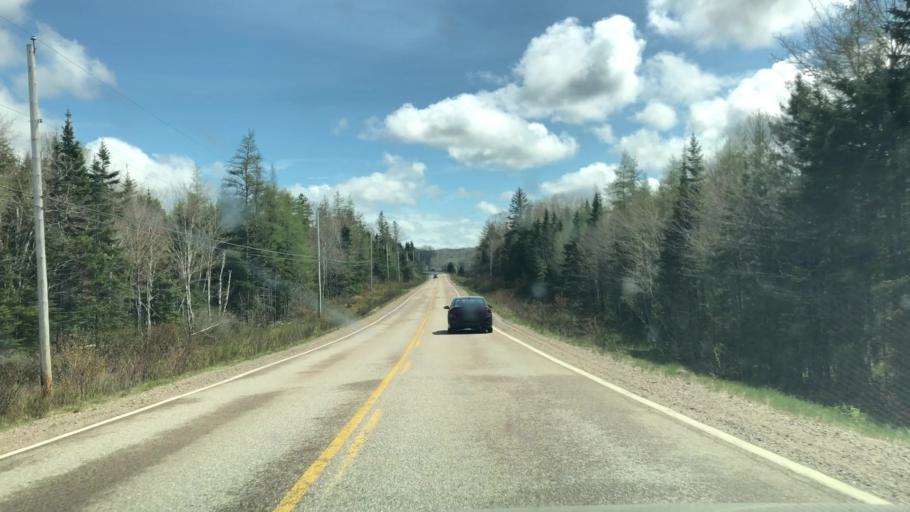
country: CA
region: Nova Scotia
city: Antigonish
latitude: 45.2060
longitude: -62.0037
